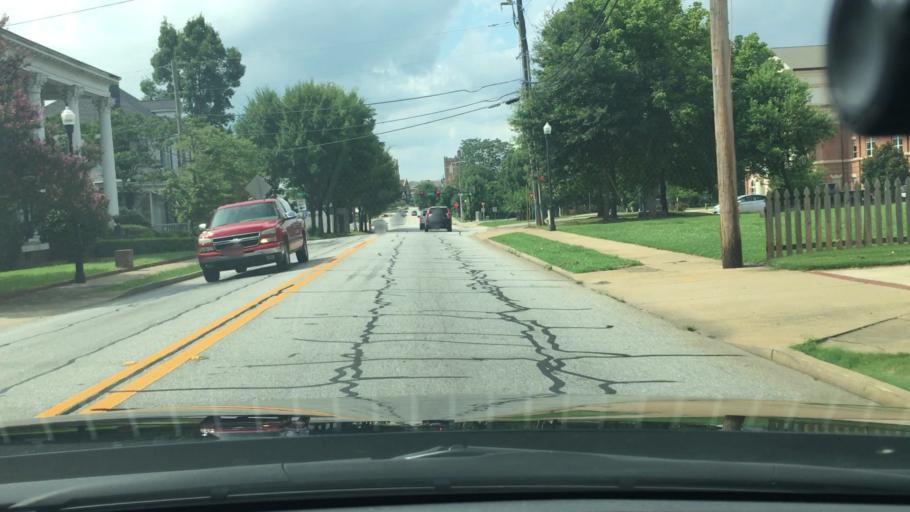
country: US
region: Georgia
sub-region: Coweta County
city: Newnan
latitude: 33.3685
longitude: -84.7989
